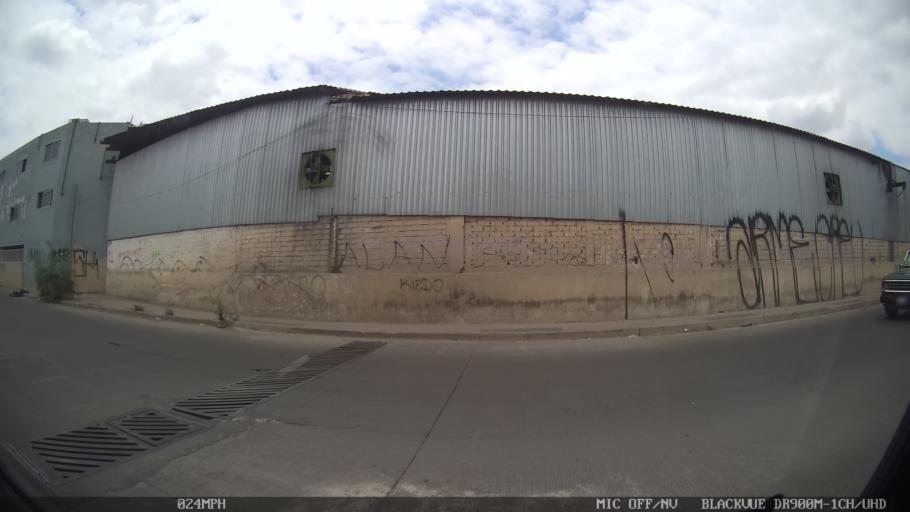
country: MX
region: Jalisco
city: Tlaquepaque
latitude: 20.6486
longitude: -103.2697
